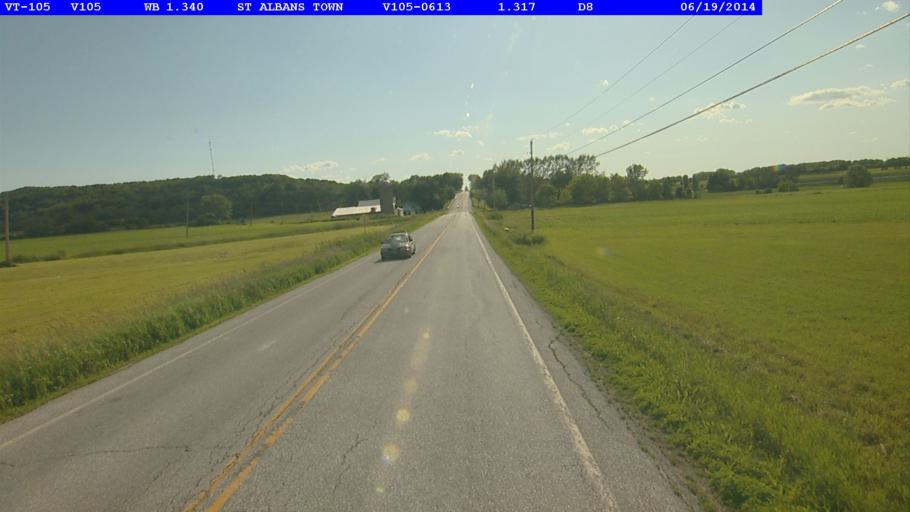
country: US
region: Vermont
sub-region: Franklin County
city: Saint Albans
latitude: 44.8287
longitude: -73.0562
